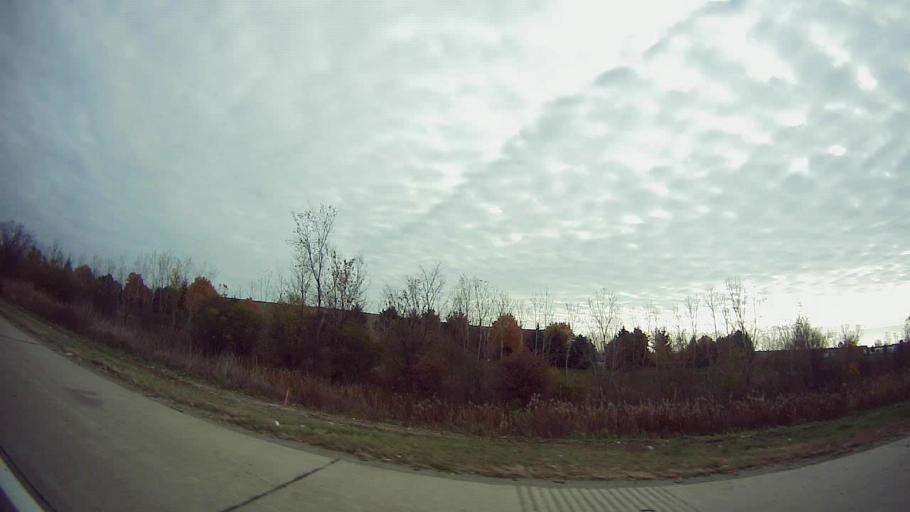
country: US
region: Michigan
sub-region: Wayne County
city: Woodhaven
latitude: 42.1775
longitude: -83.2432
